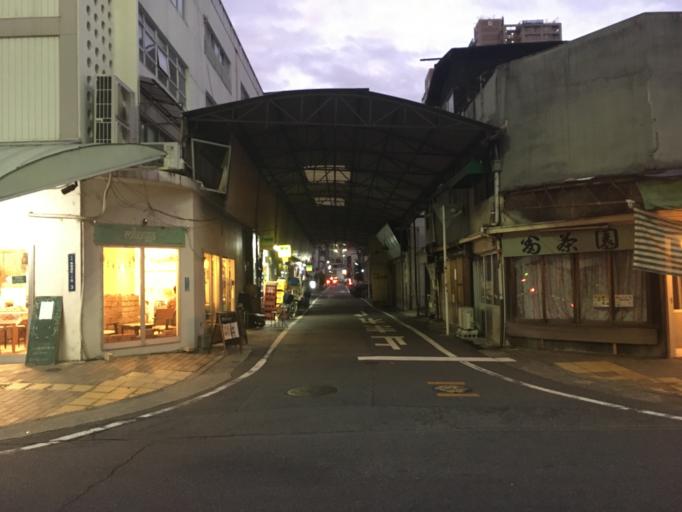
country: JP
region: Okayama
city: Okayama-shi
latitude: 34.6666
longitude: 133.9228
